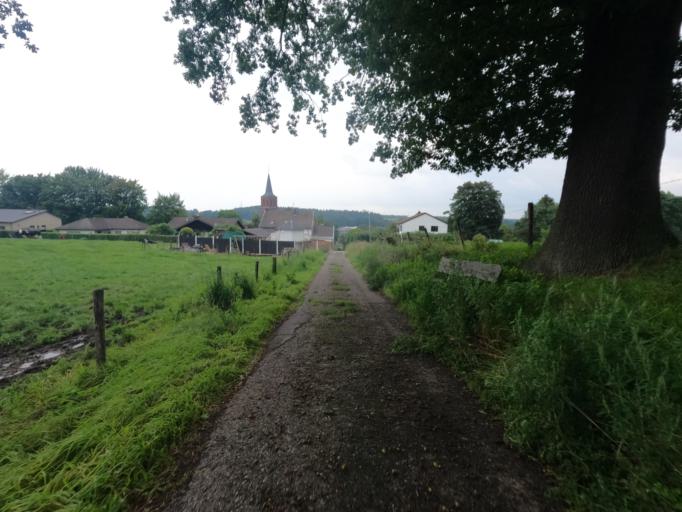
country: DE
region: North Rhine-Westphalia
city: Geilenkirchen
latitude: 50.9754
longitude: 6.1512
